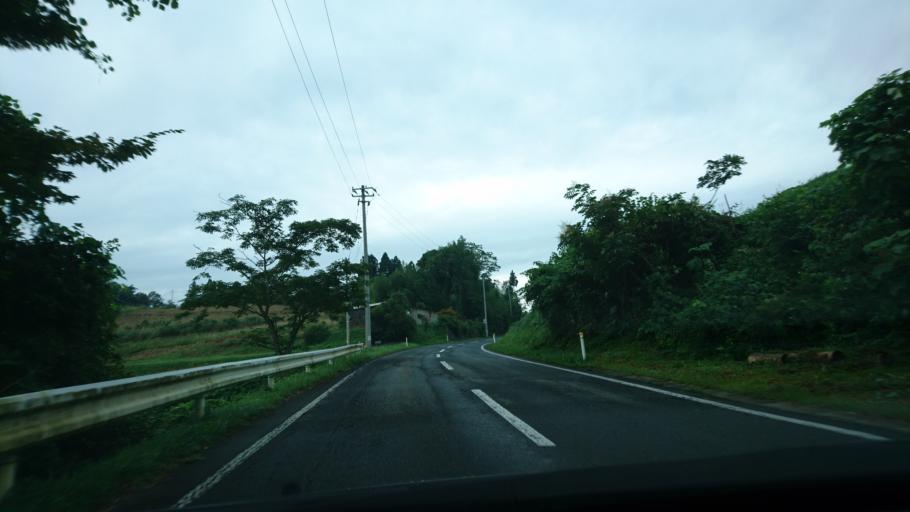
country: JP
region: Iwate
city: Ichinoseki
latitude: 39.0169
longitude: 141.2113
